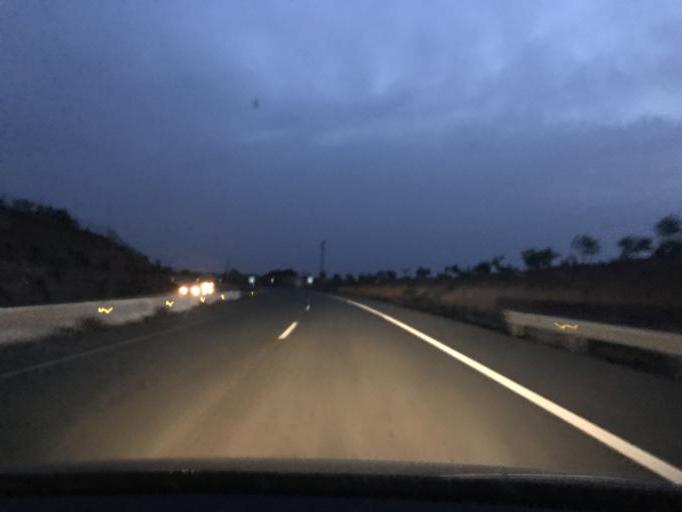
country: ES
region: Andalusia
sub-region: Provincia de Granada
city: Gor
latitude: 37.3915
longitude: -3.0021
